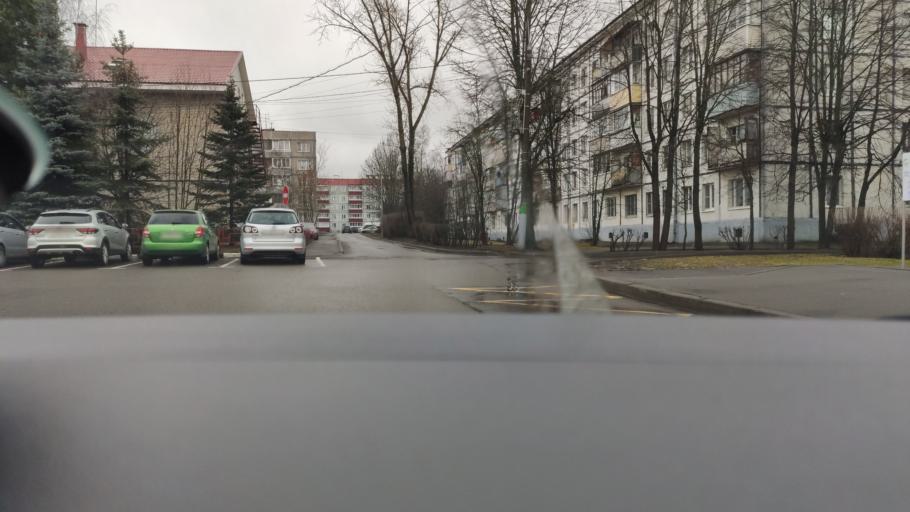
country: RU
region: Moskovskaya
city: Troitsk
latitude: 55.3196
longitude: 37.1596
